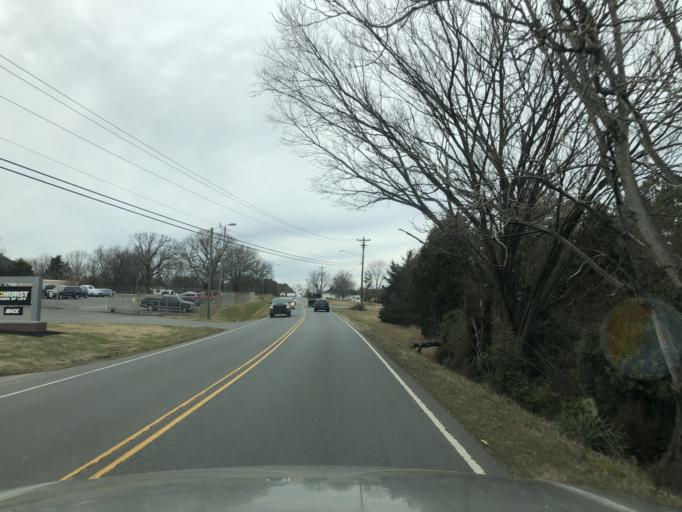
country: US
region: North Carolina
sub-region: Cleveland County
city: Shelby
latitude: 35.2997
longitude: -81.4856
